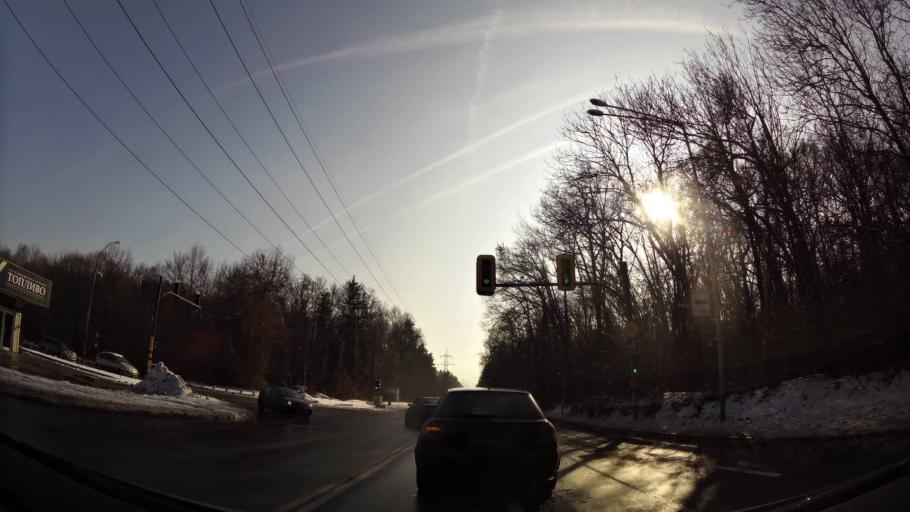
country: BG
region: Sofia-Capital
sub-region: Stolichna Obshtina
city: Sofia
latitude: 42.6669
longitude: 23.3376
